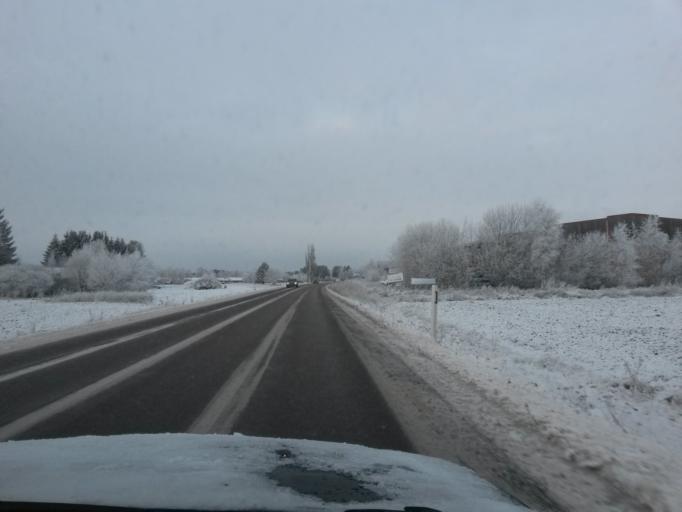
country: SE
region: Vaestra Goetaland
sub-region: Vara Kommun
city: Vara
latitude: 58.3220
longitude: 12.9335
